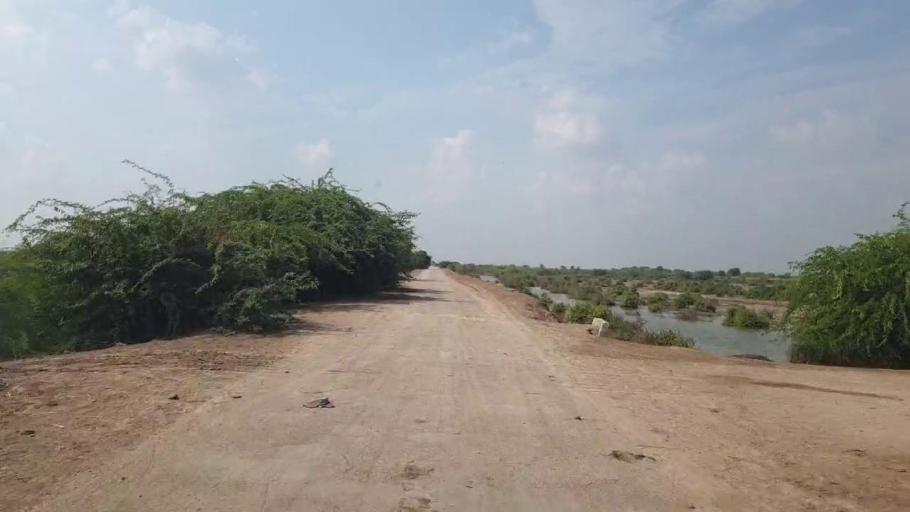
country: PK
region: Sindh
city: Badin
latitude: 24.5066
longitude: 68.6280
